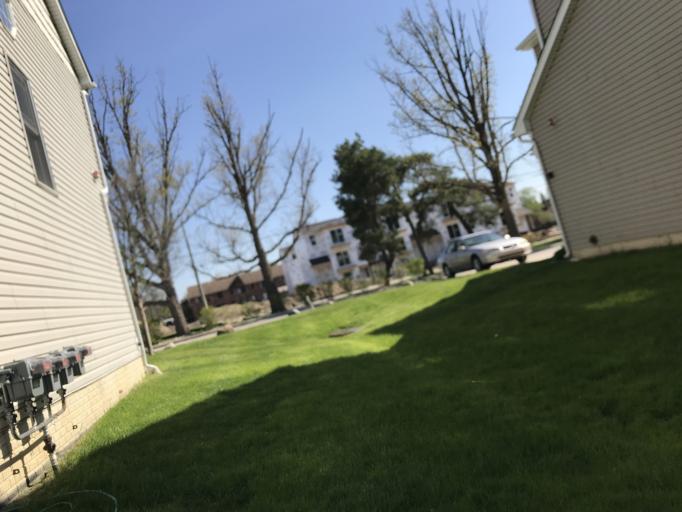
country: US
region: Michigan
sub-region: Oakland County
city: Farmington
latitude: 42.4639
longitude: -83.3364
